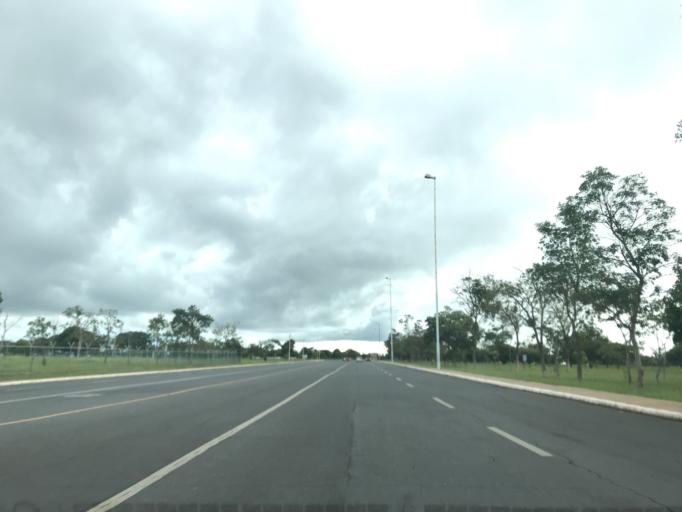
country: BR
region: Federal District
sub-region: Brasilia
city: Brasilia
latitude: -15.7770
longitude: -47.9214
